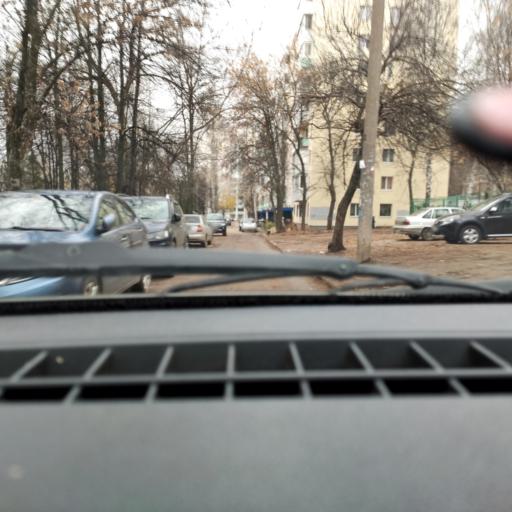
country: RU
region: Bashkortostan
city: Ufa
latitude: 54.7450
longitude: 56.0222
